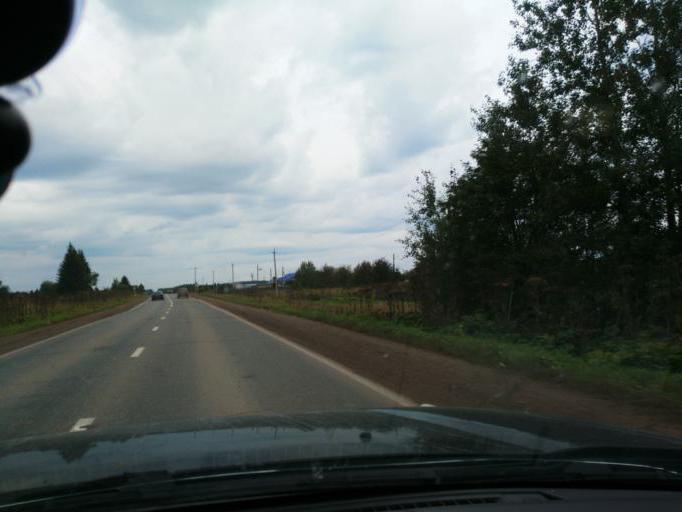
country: RU
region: Perm
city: Chernushka
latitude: 56.7357
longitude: 56.1721
